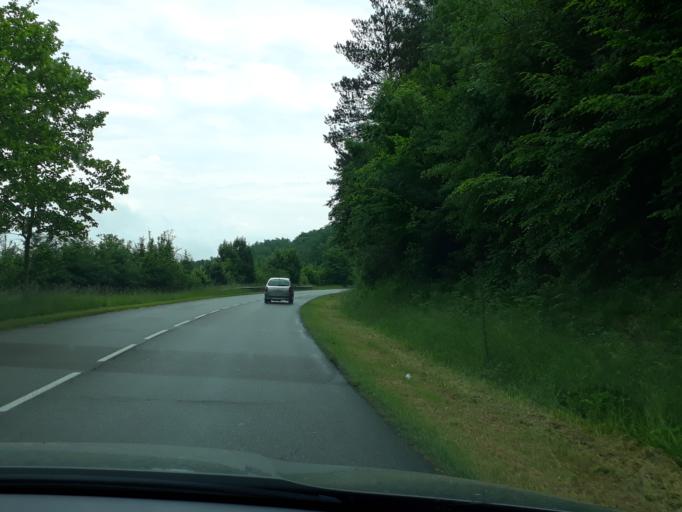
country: FR
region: Limousin
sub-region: Departement de la Correze
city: Cosnac
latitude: 45.1537
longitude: 1.6191
